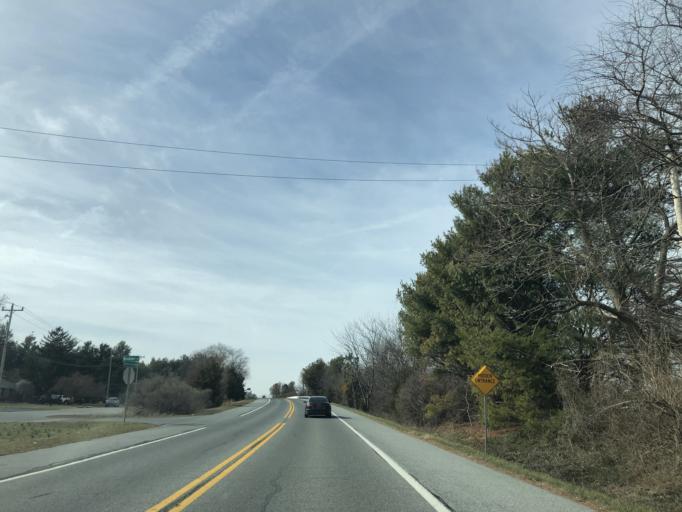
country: US
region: Delaware
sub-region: Kent County
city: Smyrna
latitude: 39.2914
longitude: -75.5908
